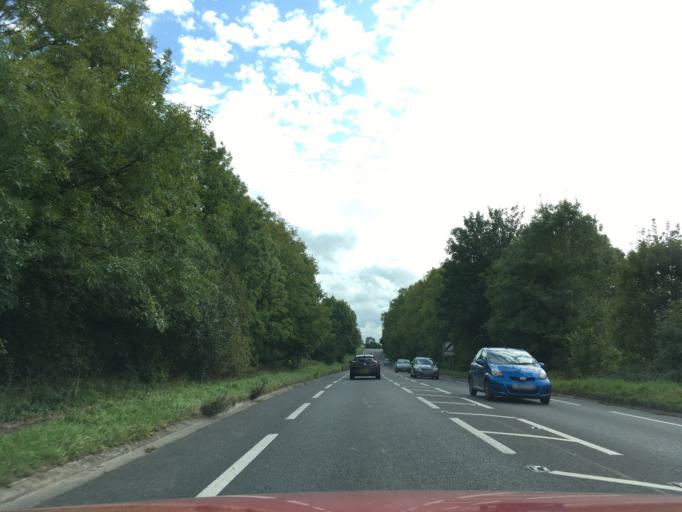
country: GB
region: England
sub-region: Gloucestershire
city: Berkeley
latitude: 51.6751
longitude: -2.4367
